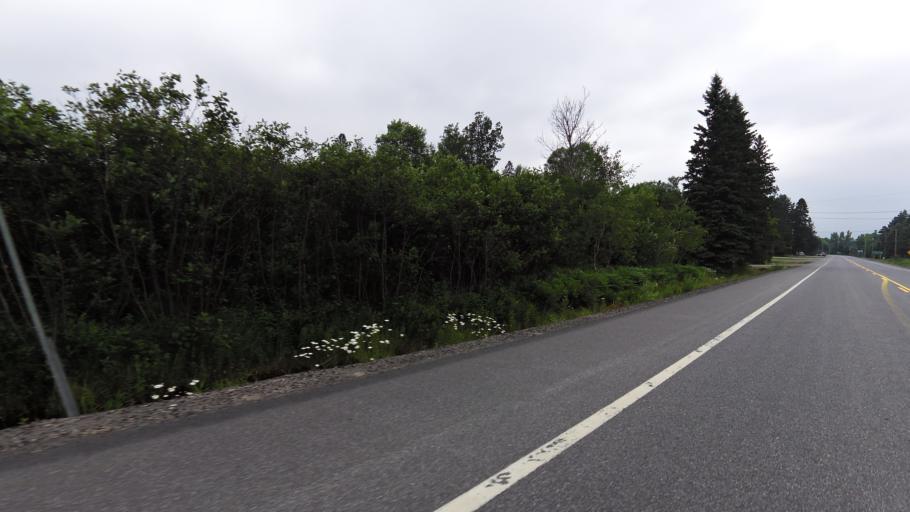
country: CA
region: Ontario
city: Huntsville
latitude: 45.3642
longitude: -78.9284
